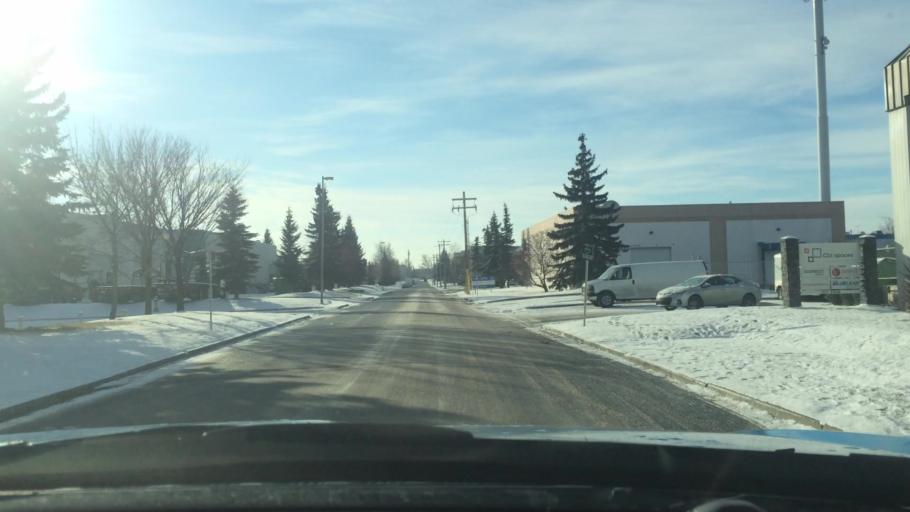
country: CA
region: Alberta
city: Calgary
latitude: 51.1177
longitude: -114.0447
